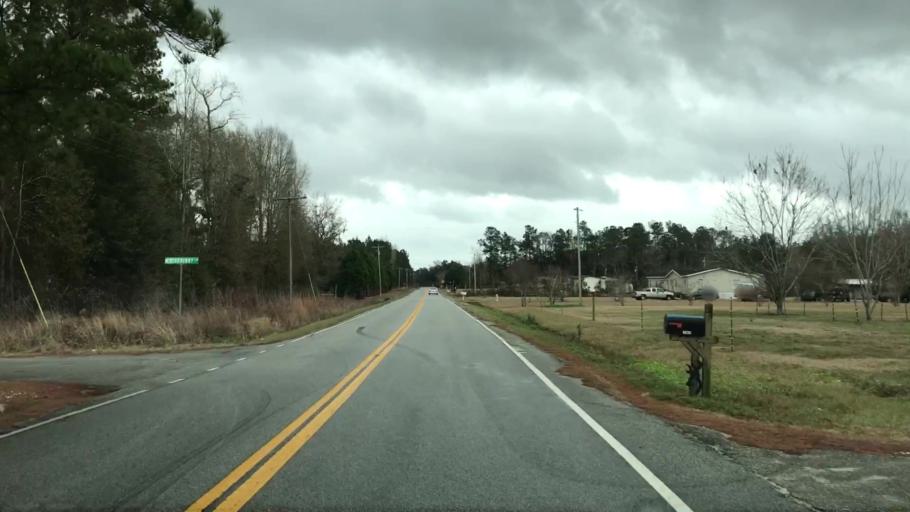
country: US
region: South Carolina
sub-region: Williamsburg County
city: Andrews
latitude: 33.4926
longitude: -79.5051
